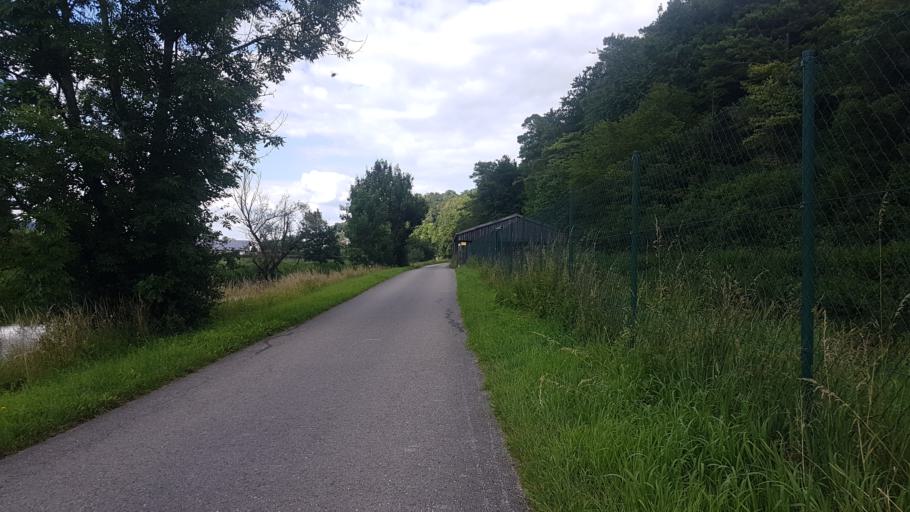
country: DE
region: Bavaria
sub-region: Regierungsbezirk Mittelfranken
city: Treuchtlingen
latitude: 48.9381
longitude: 10.9316
